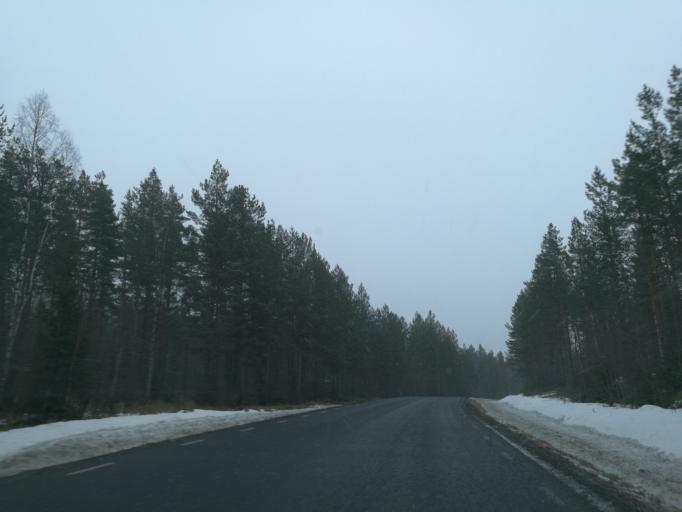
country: NO
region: Hedmark
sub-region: Grue
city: Kirkenaer
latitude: 60.6985
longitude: 12.6196
